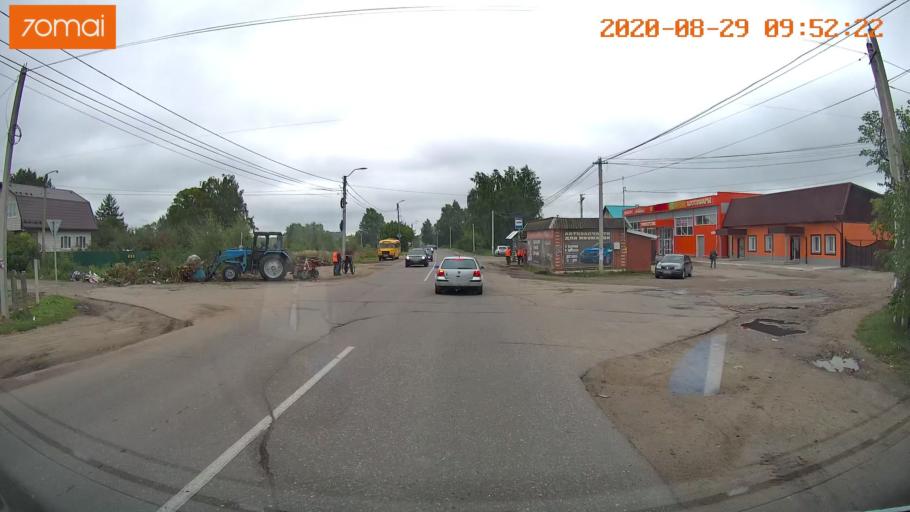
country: RU
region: Ivanovo
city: Kineshma
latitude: 57.4240
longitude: 42.2084
